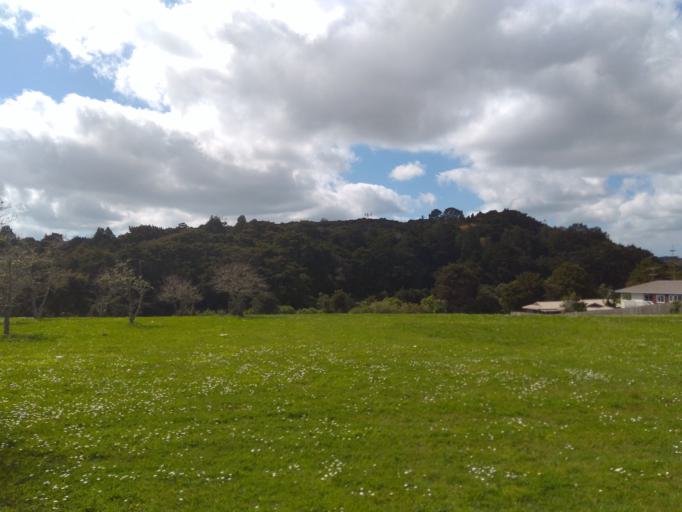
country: NZ
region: Auckland
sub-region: Auckland
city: Rothesay Bay
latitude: -36.7372
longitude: 174.6937
